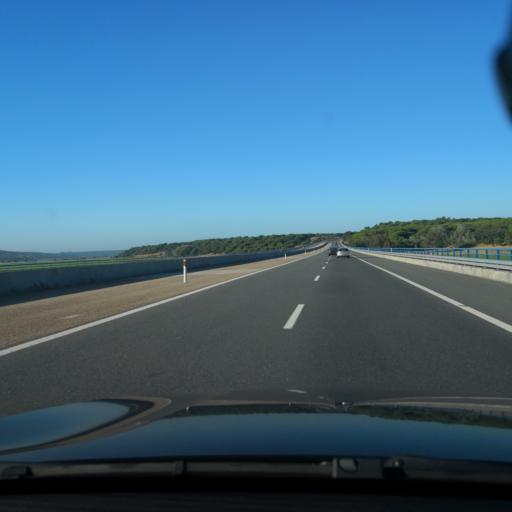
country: PT
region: Setubal
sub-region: Alcacer do Sal
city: Alcacer do Sal
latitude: 38.3588
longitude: -8.4924
